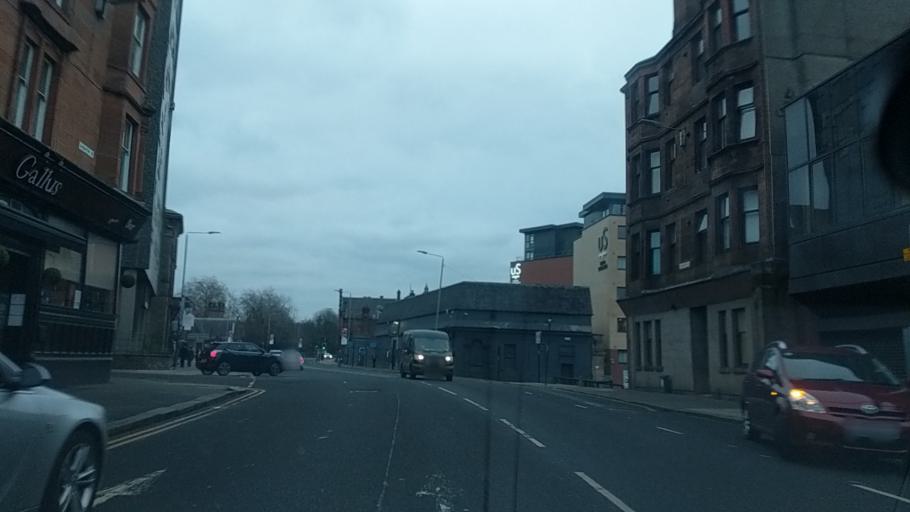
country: GB
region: Scotland
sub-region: Glasgow City
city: Glasgow
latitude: 55.8701
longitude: -4.2980
